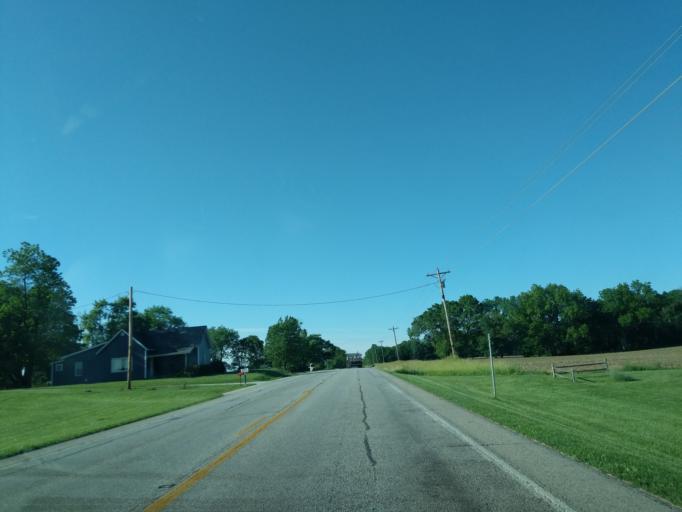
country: US
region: Indiana
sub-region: Shelby County
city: Morristown
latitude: 39.6562
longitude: -85.7728
